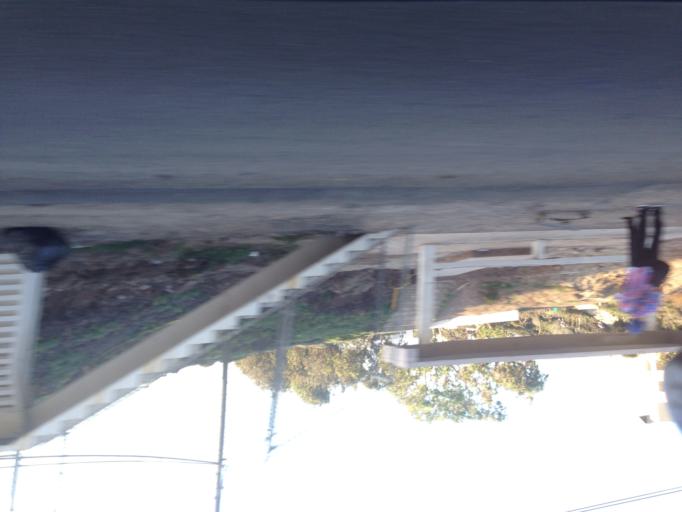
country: MX
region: Baja California
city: El Sauzal
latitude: 31.8665
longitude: -116.6679
